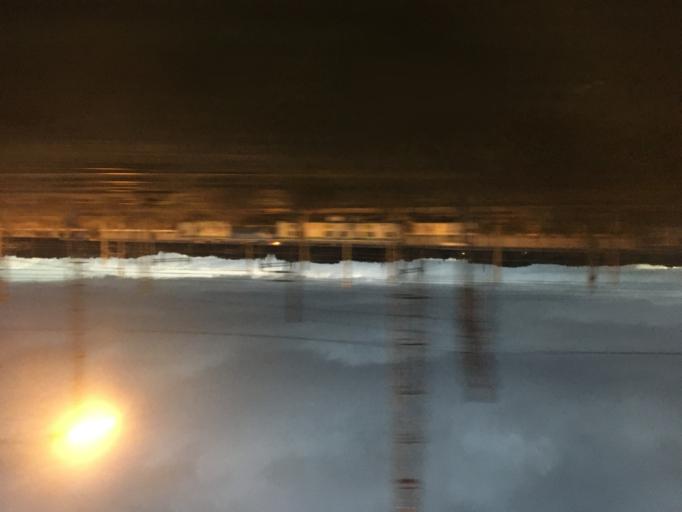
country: JP
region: Aomori
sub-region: Hachinohe Shi
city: Uchimaru
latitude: 40.5164
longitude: 141.4395
